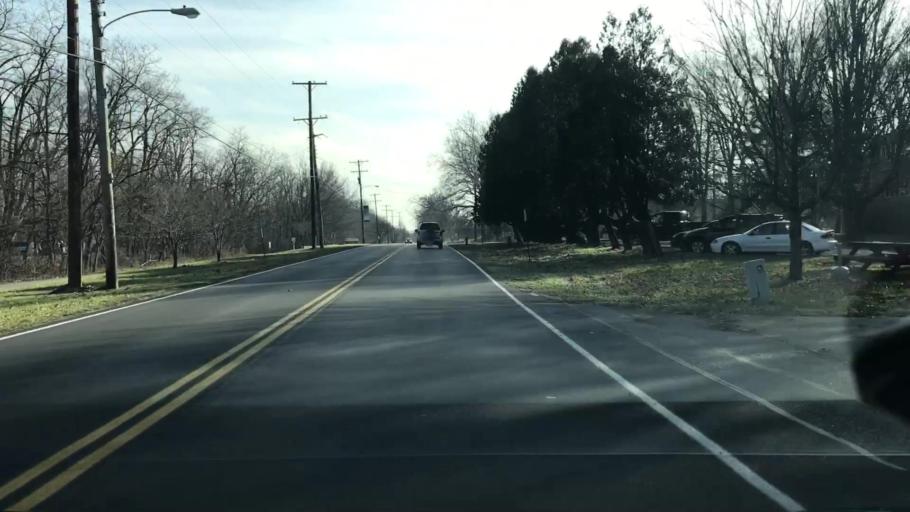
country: US
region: Ohio
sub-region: Greene County
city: Yellow Springs
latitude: 39.8017
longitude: -83.8863
